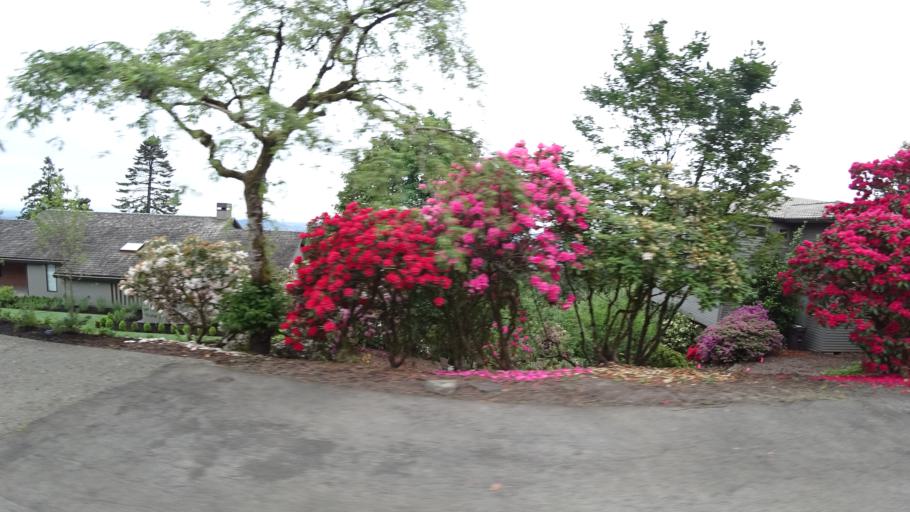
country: US
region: Oregon
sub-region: Multnomah County
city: Portland
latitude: 45.4873
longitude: -122.6926
